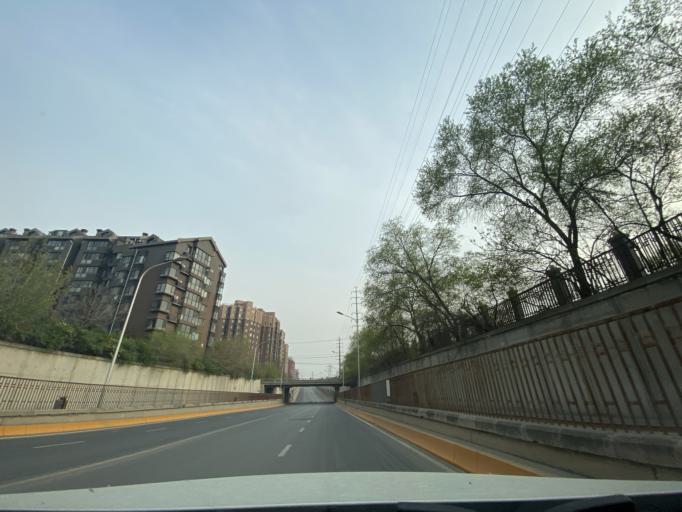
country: CN
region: Beijing
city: Babaoshan
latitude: 39.9319
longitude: 116.2325
